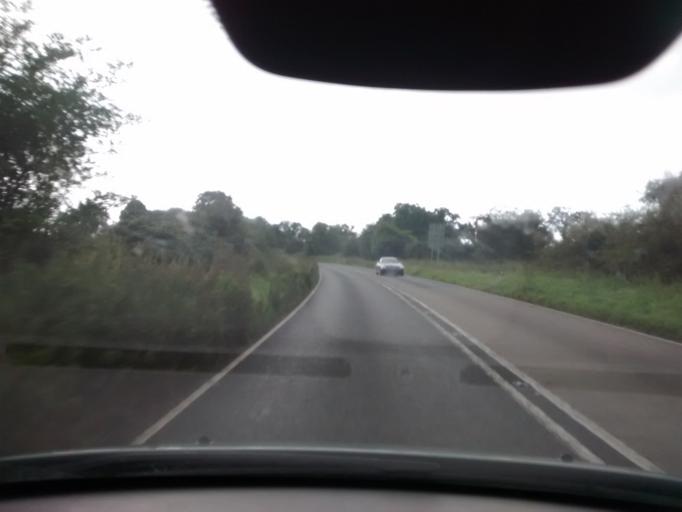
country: GB
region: England
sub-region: Hampshire
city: Fordingbridge
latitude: 50.8933
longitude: -1.7853
